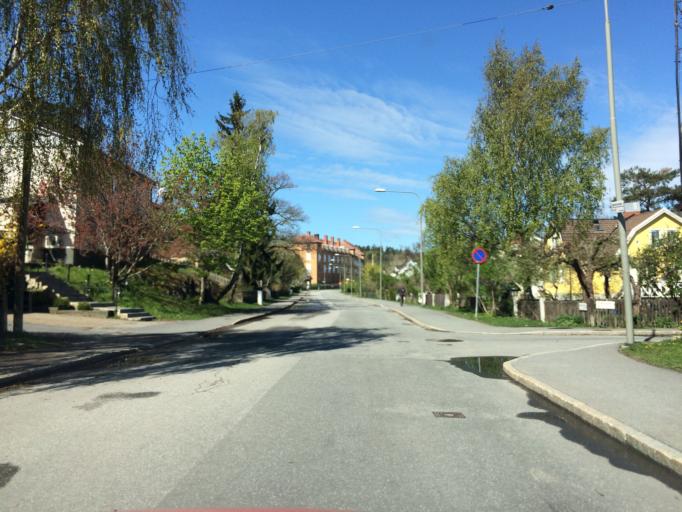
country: SE
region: Stockholm
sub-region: Huddinge Kommun
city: Segeltorp
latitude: 59.2958
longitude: 17.9622
